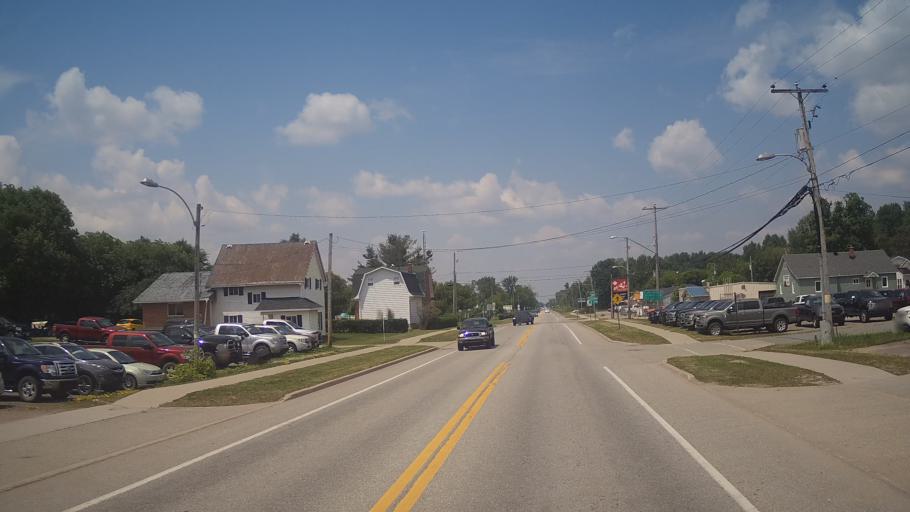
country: CA
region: Quebec
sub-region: Outaouais
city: Shawville
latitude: 45.5994
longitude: -76.4930
